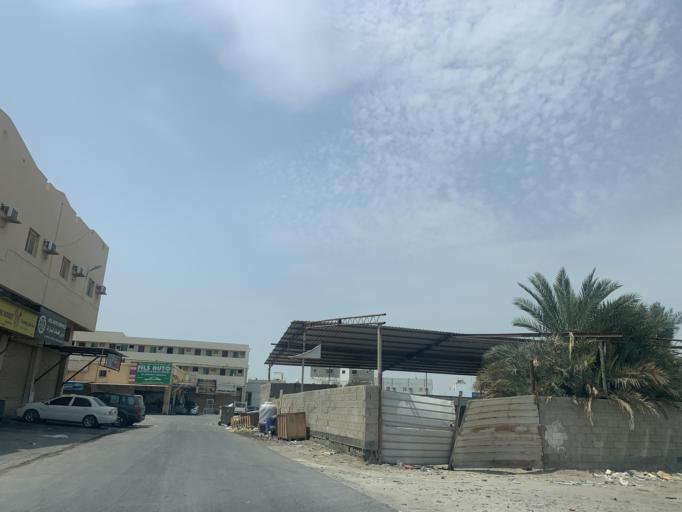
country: BH
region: Central Governorate
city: Madinat Hamad
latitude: 26.1418
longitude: 50.4897
